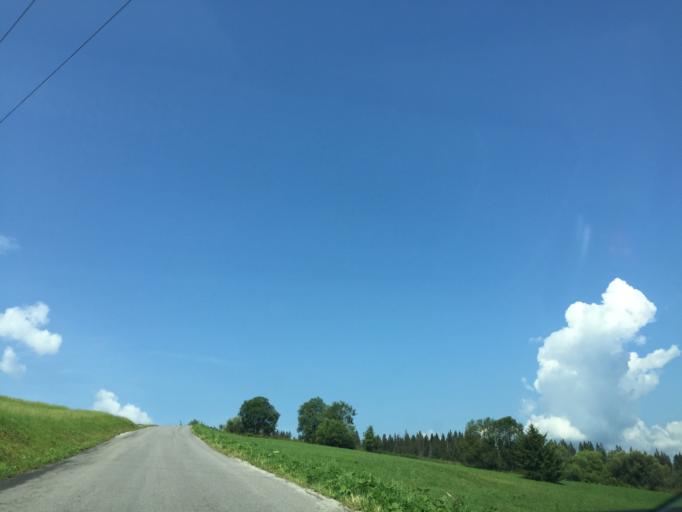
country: PL
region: Silesian Voivodeship
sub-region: Powiat zywiecki
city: Sopotnia Wielka
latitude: 49.4339
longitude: 19.3101
